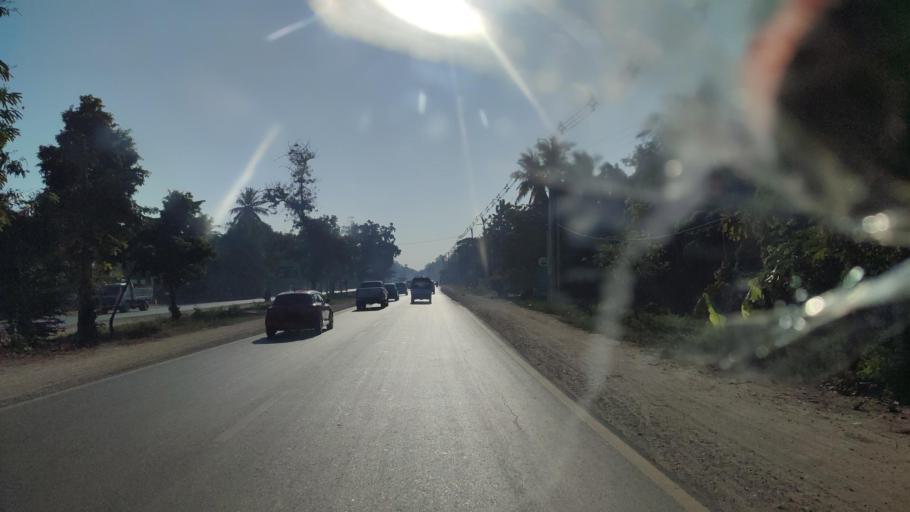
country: MM
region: Mandalay
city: Mandalay
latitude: 21.9174
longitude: 96.1648
